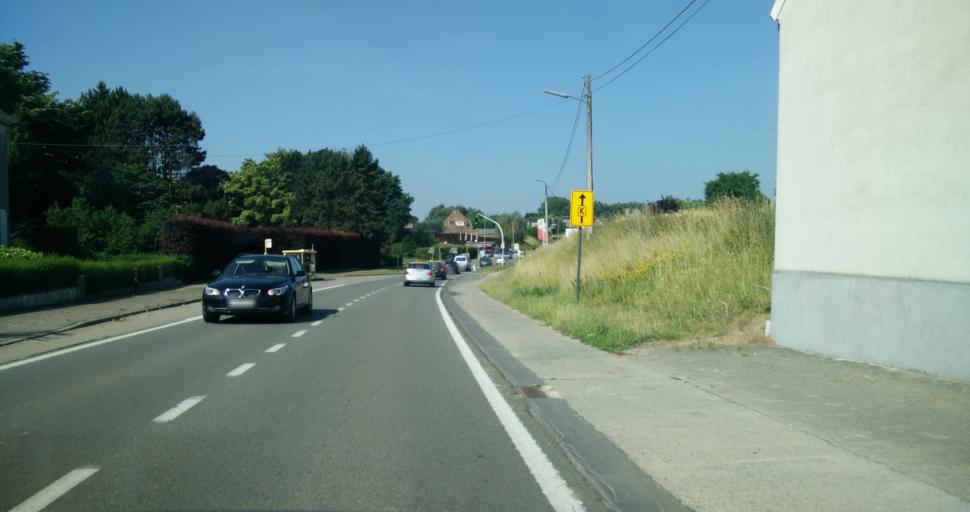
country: BE
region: Flanders
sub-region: Provincie Oost-Vlaanderen
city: Zottegem
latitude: 50.8859
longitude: 3.7830
